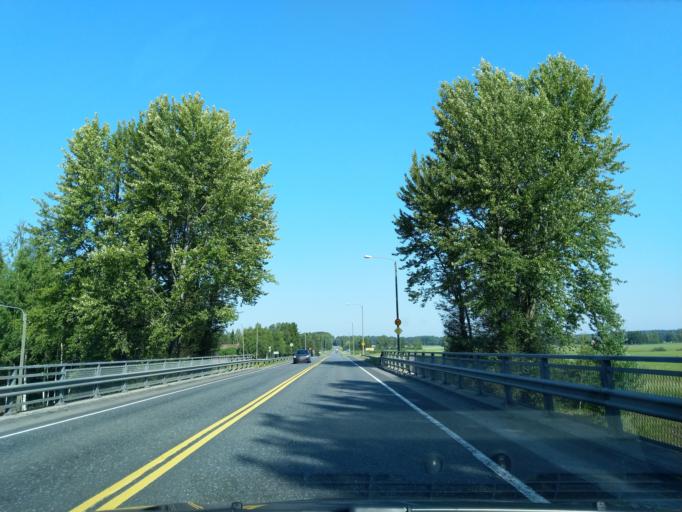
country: FI
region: Haeme
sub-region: Forssa
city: Humppila
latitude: 60.9534
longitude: 23.3395
